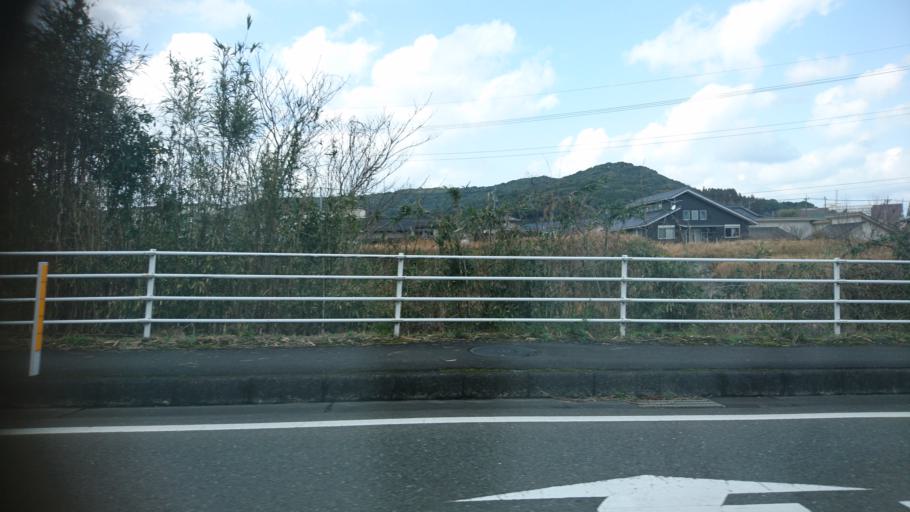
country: JP
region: Kagoshima
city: Satsumasendai
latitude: 31.7966
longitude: 130.3055
